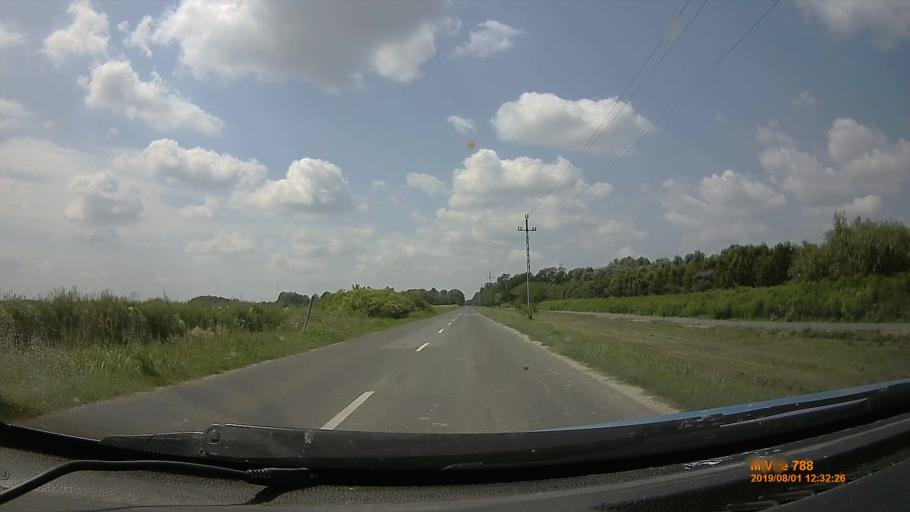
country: HU
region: Baranya
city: Harkany
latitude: 45.8556
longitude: 18.2662
